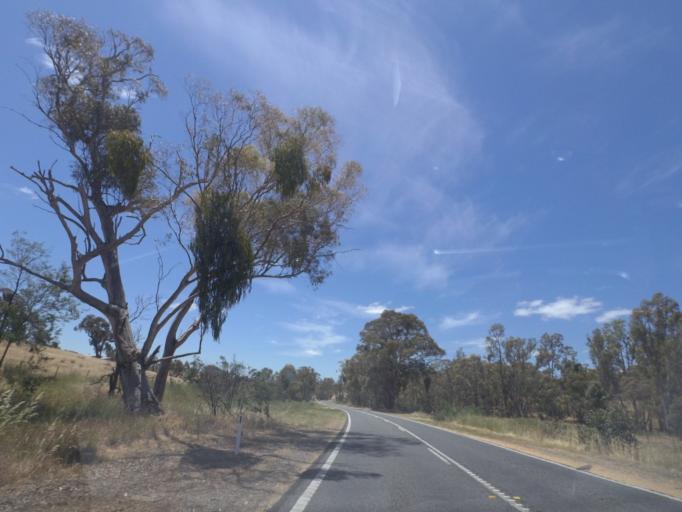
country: AU
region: Victoria
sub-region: Mount Alexander
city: Castlemaine
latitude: -37.1998
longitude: 144.1457
